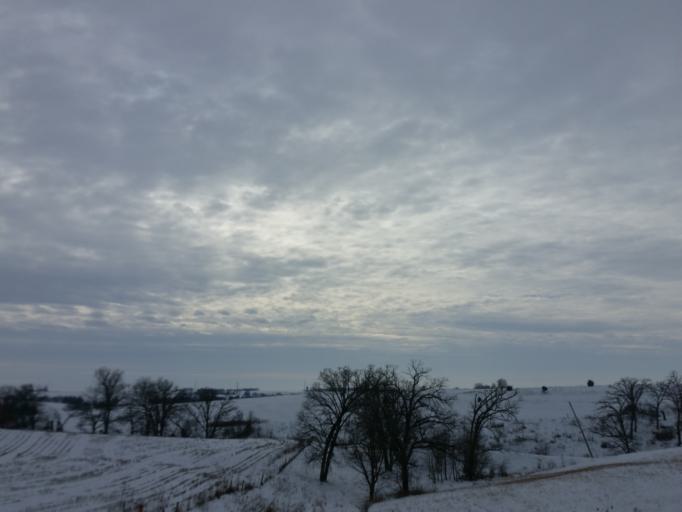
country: US
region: Iowa
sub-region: Dubuque County
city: Asbury
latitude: 42.3821
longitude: -90.7326
